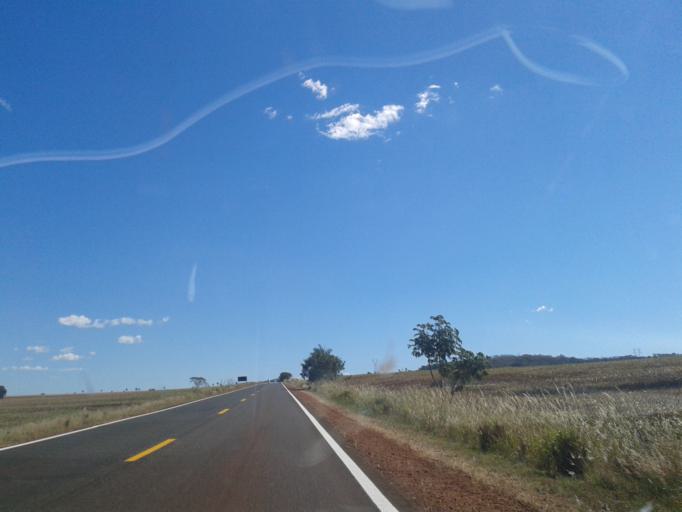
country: BR
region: Minas Gerais
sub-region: Capinopolis
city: Capinopolis
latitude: -18.6901
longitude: -49.4328
